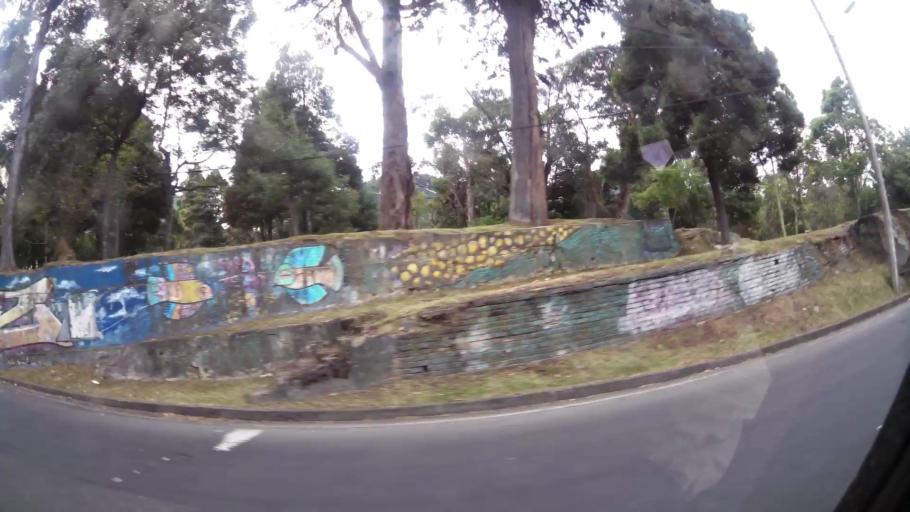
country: CO
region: Bogota D.C.
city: Bogota
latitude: 4.6258
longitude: -74.0634
